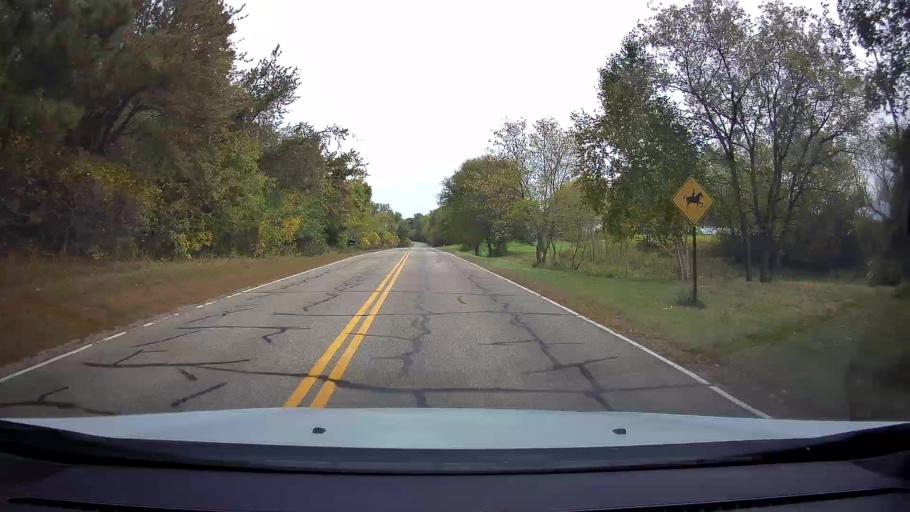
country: US
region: Minnesota
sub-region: Washington County
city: Stillwater
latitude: 45.1044
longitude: -92.8026
